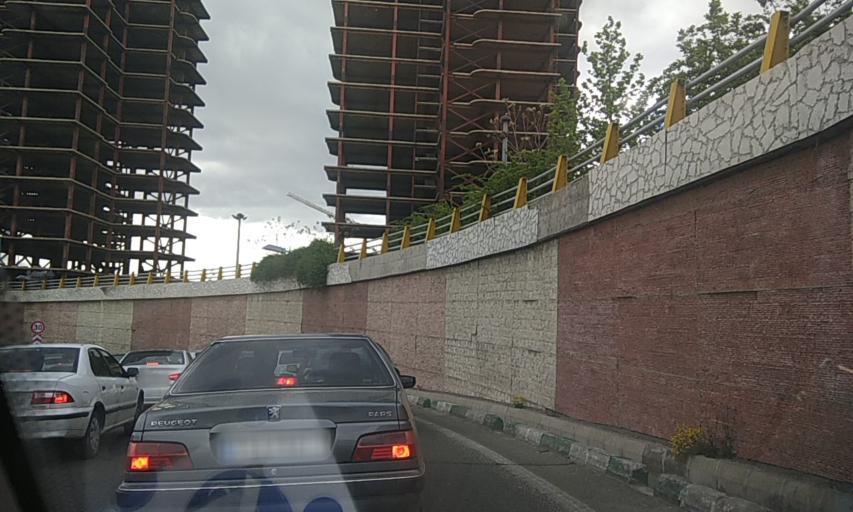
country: IR
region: Tehran
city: Tajrish
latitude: 35.7729
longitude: 51.3448
